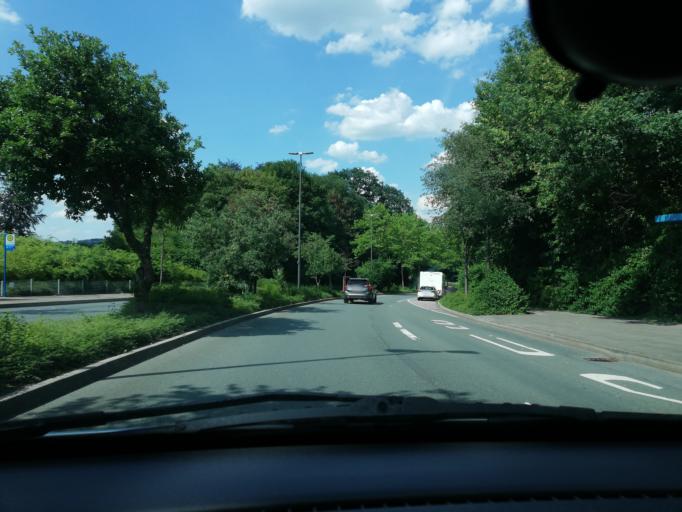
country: DE
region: North Rhine-Westphalia
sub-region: Regierungsbezirk Dusseldorf
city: Wuppertal
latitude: 51.2514
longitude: 7.1605
